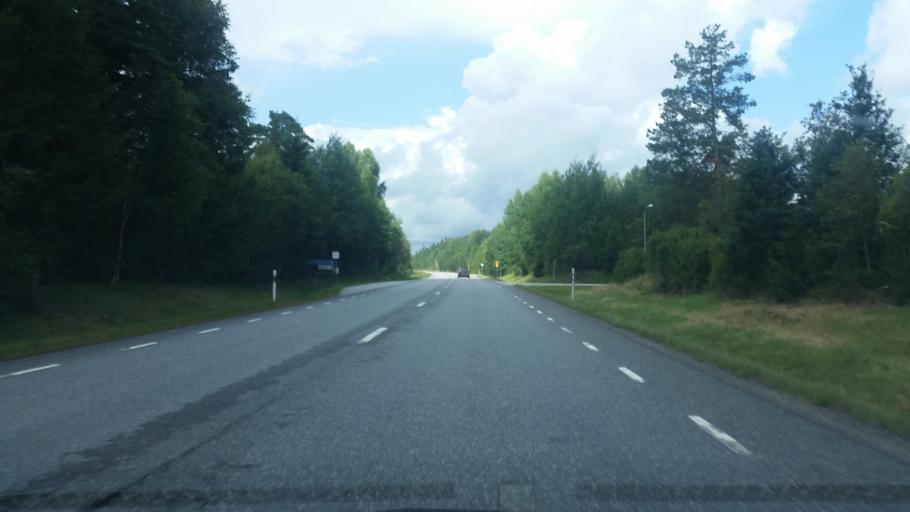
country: SE
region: Vaestra Goetaland
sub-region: Tranemo Kommun
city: Langhem
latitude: 57.5871
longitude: 13.2103
